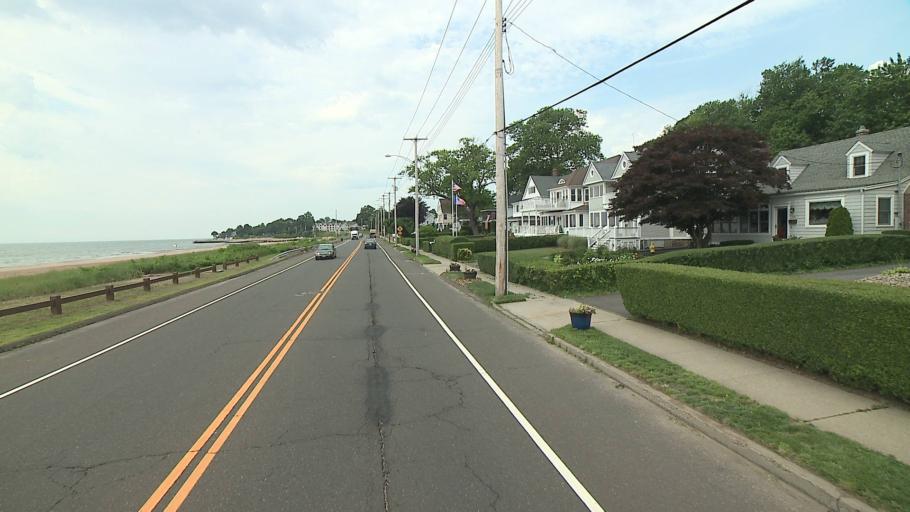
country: US
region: Connecticut
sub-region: New Haven County
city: Woodmont
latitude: 41.2459
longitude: -72.9675
